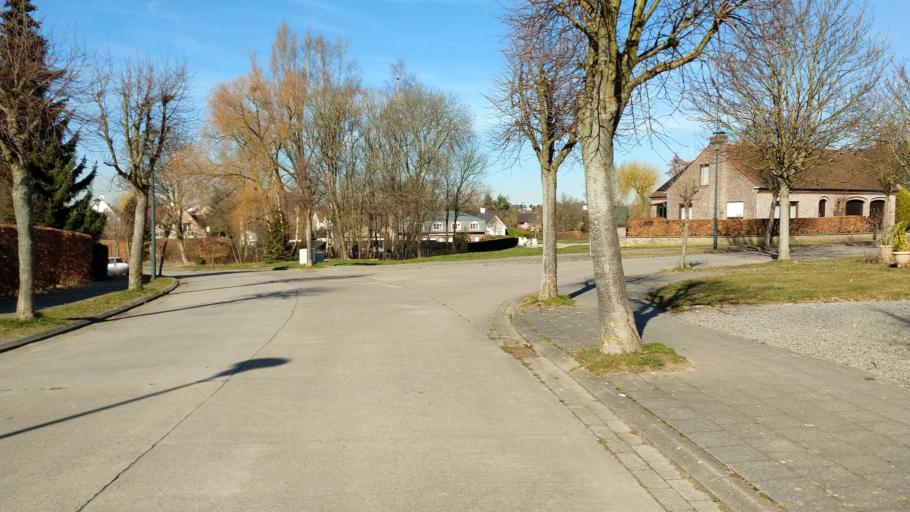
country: BE
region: Flanders
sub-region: Provincie Vlaams-Brabant
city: Wezembeek-Oppem
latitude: 50.8571
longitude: 4.5023
